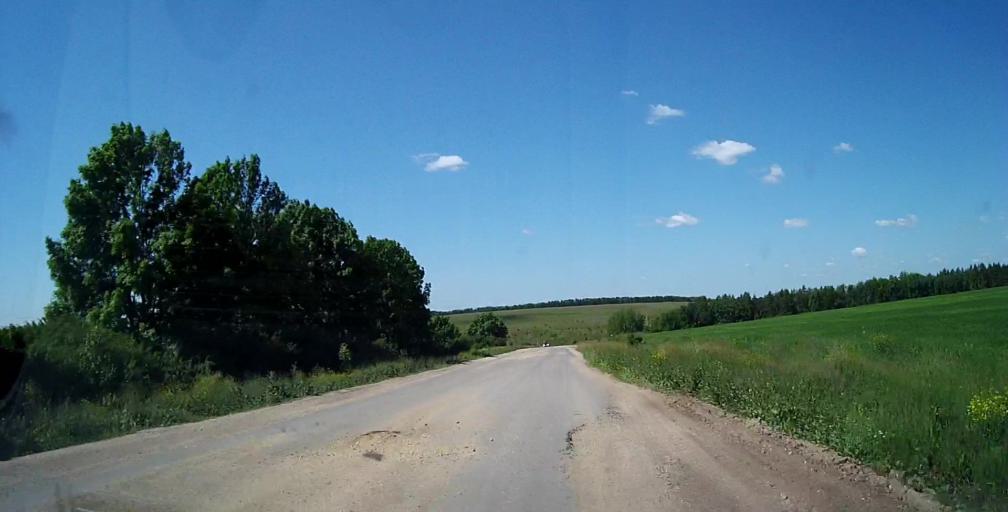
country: RU
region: Tula
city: Kurkino
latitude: 53.1995
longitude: 38.5812
